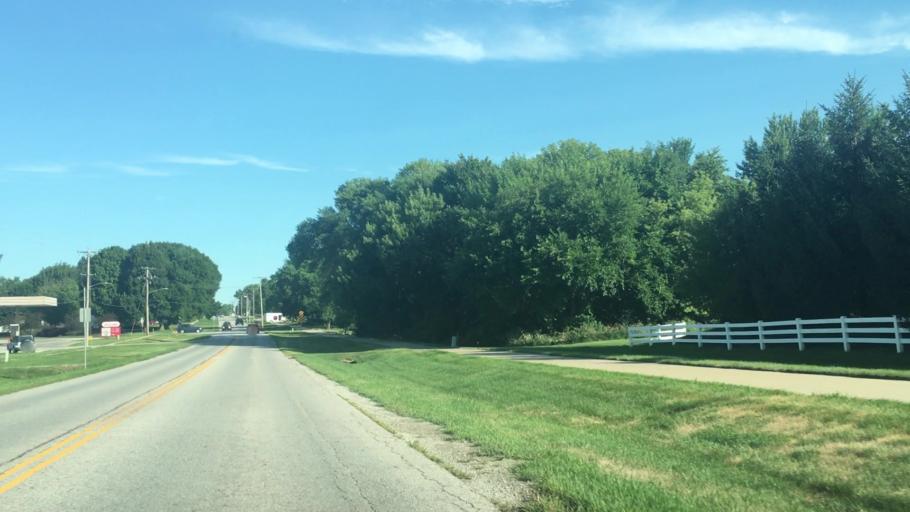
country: US
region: Iowa
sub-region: Johnson County
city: North Liberty
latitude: 41.7437
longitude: -91.5912
